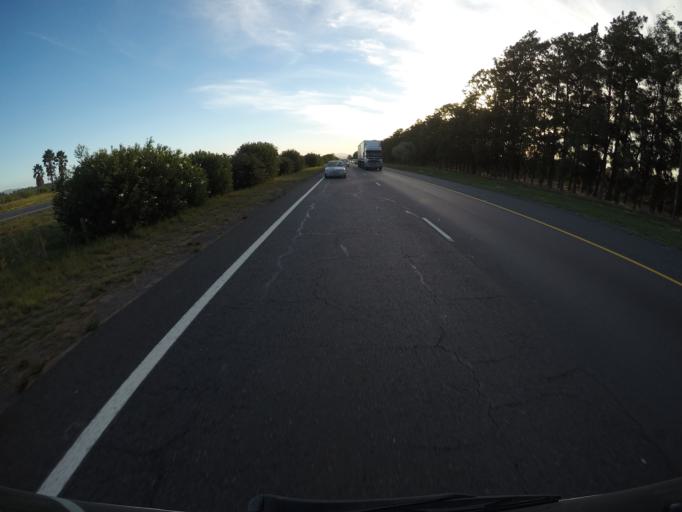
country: ZA
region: Western Cape
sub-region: City of Cape Town
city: Kraaifontein
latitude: -33.8247
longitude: 18.7738
